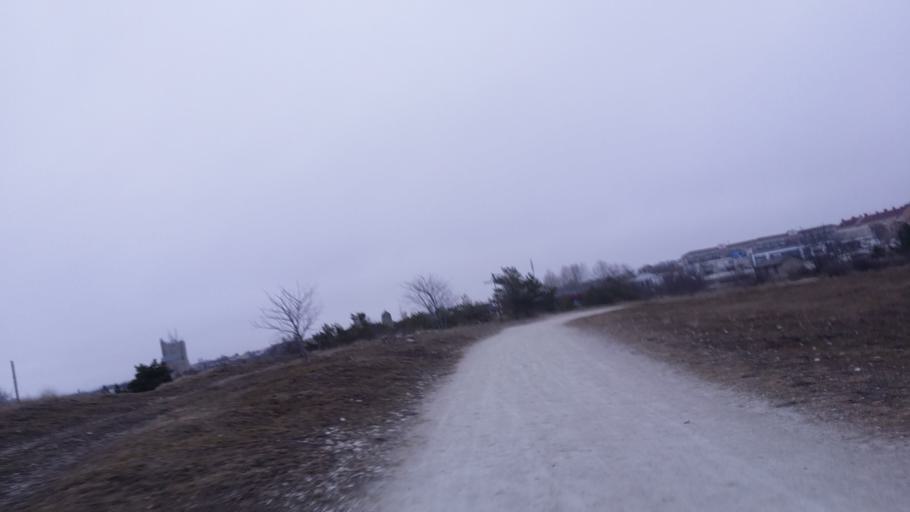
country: SE
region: Gotland
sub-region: Gotland
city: Vibble
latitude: 57.6224
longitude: 18.2702
